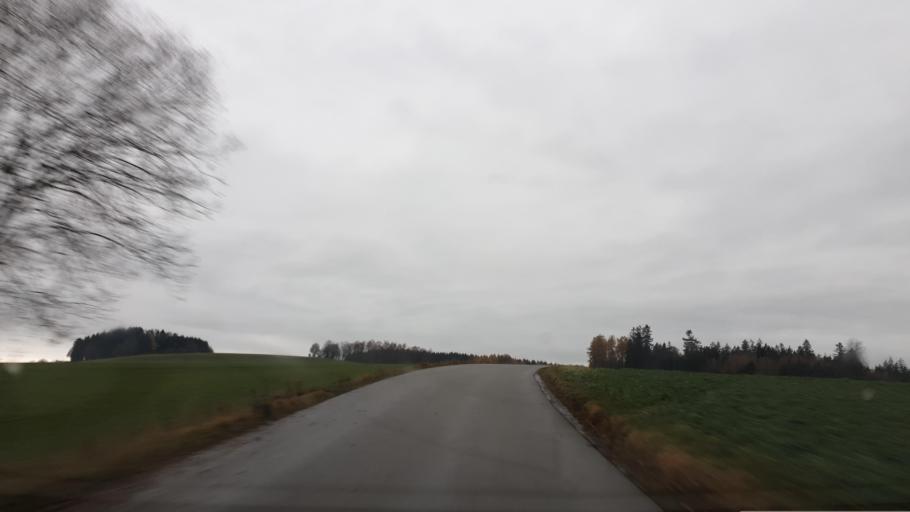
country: DE
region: Saxony
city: Zwonitz
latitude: 50.6481
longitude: 12.7985
